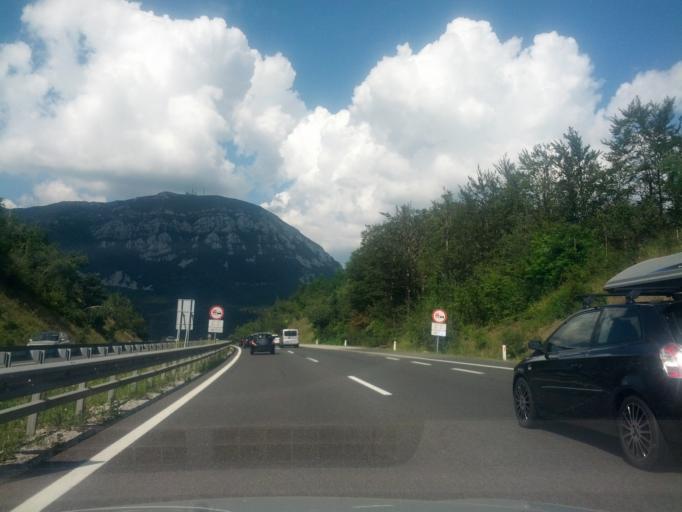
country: SI
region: Divaca
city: Divaca
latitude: 45.7458
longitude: 14.0413
